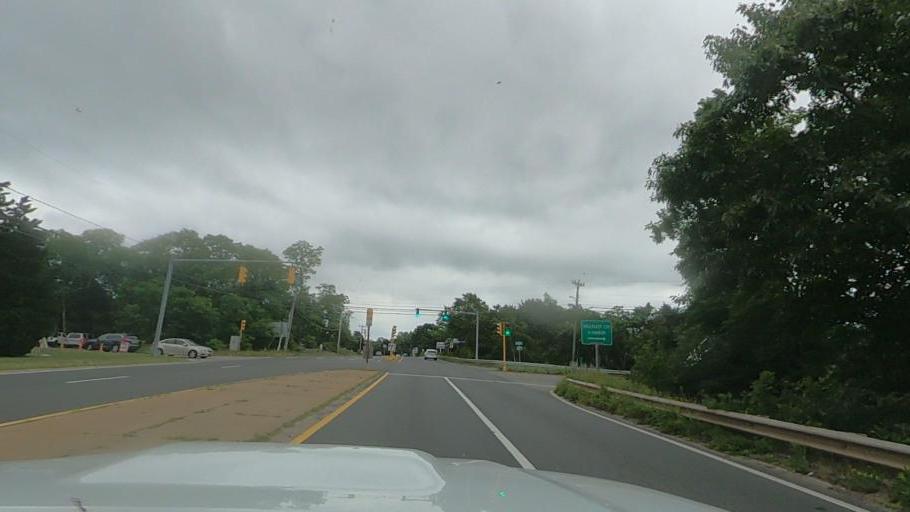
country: US
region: Massachusetts
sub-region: Barnstable County
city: Wellfleet
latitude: 41.9375
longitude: -70.0216
